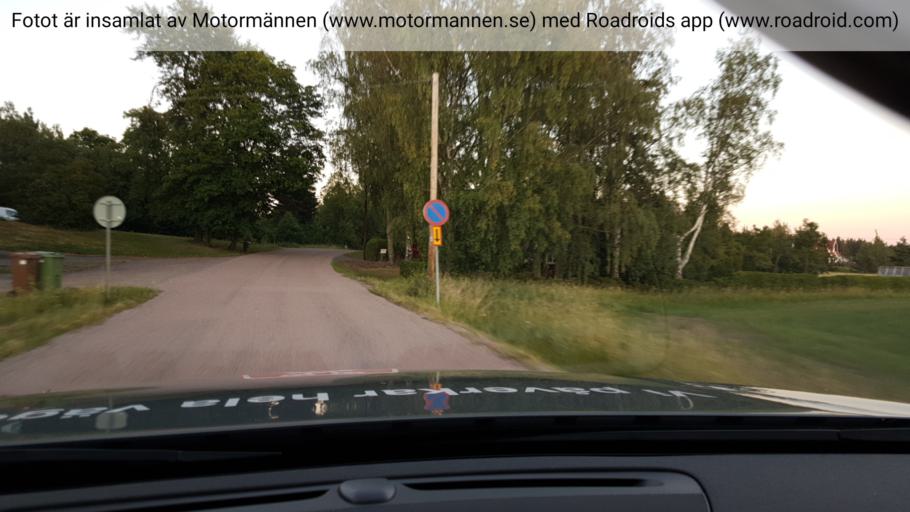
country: SE
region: Vaestmanland
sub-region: Hallstahammars Kommun
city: Kolback
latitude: 59.5344
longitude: 16.1508
